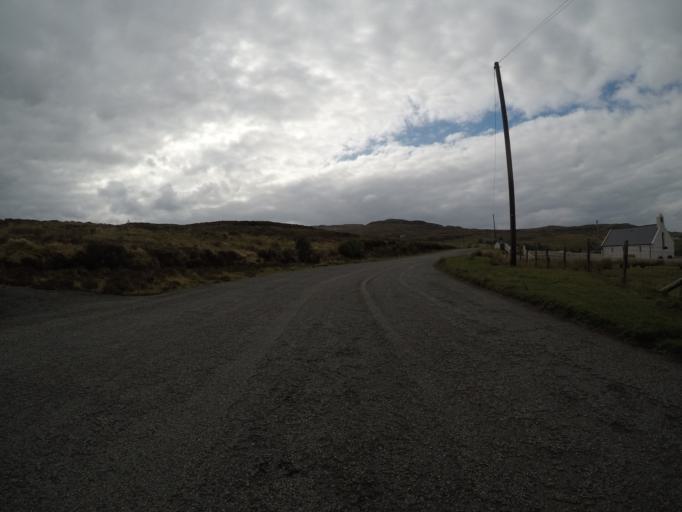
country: GB
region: Scotland
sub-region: Highland
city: Isle of Skye
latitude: 57.2966
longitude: -6.3498
